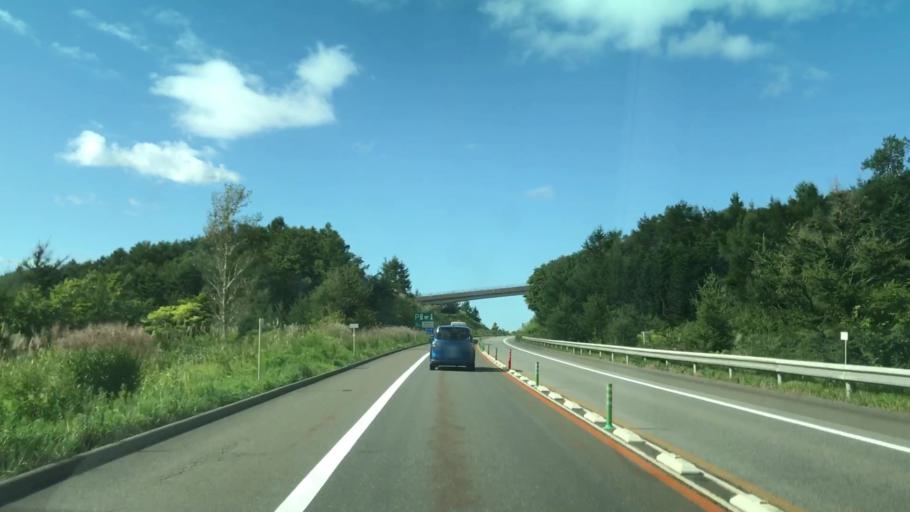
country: JP
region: Hokkaido
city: Date
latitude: 42.4439
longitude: 140.9153
